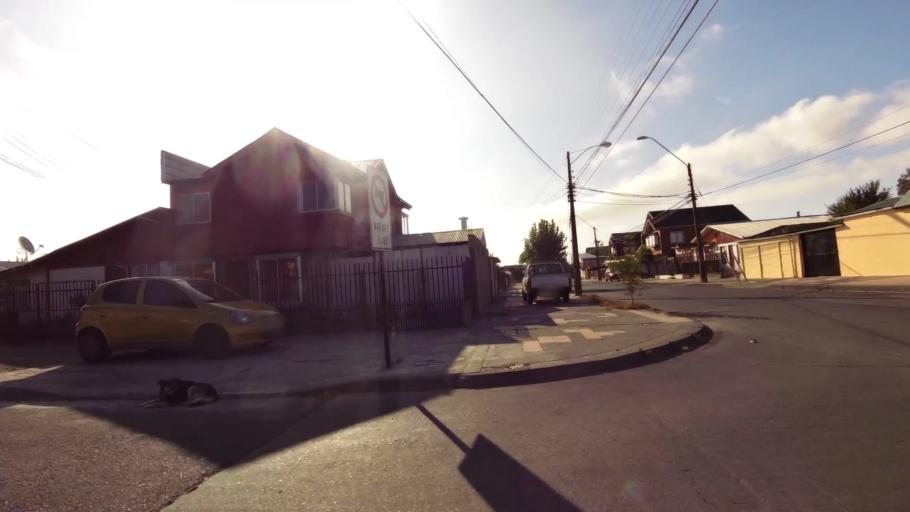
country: CL
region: Biobio
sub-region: Provincia de Concepcion
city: Concepcion
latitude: -36.7941
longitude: -73.1055
